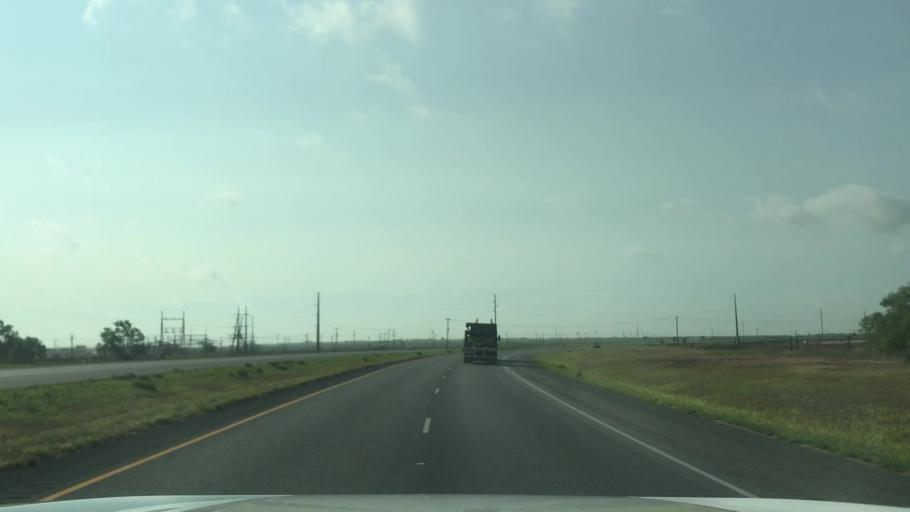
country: US
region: Texas
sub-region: Scurry County
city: Snyder
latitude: 32.7854
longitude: -100.9486
